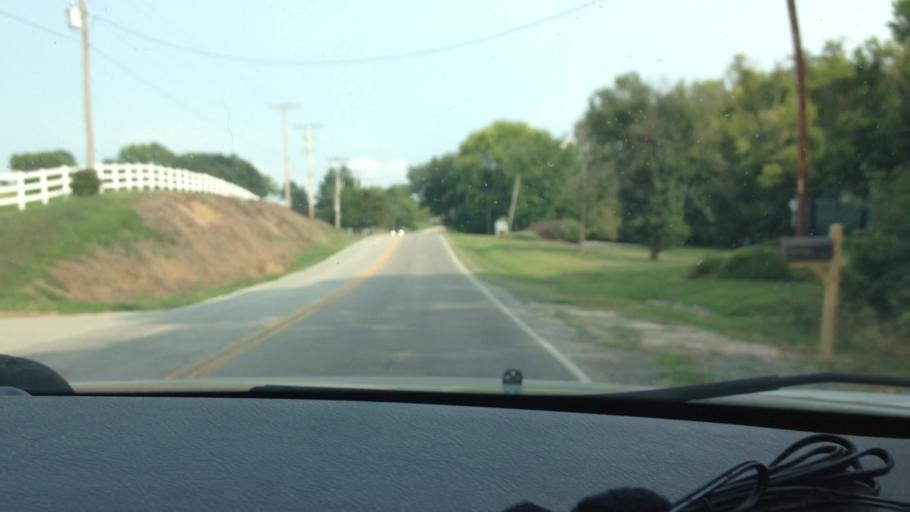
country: US
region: Missouri
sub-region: Platte County
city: Weston
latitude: 39.4074
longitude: -94.8821
